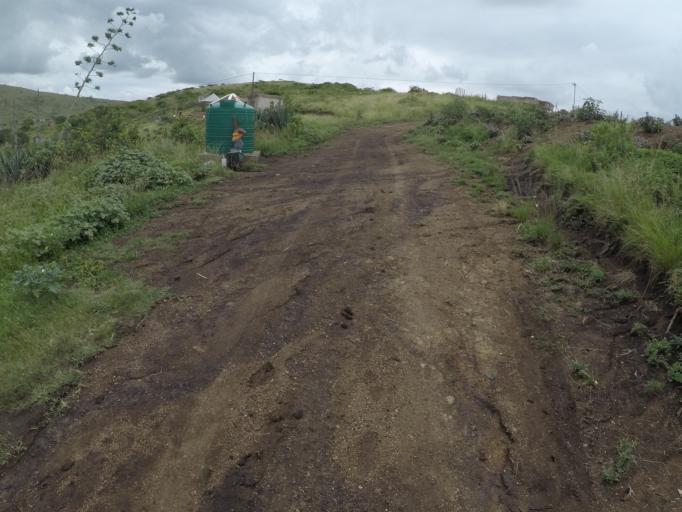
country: ZA
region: KwaZulu-Natal
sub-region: uThungulu District Municipality
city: Empangeni
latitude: -28.7066
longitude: 31.8515
